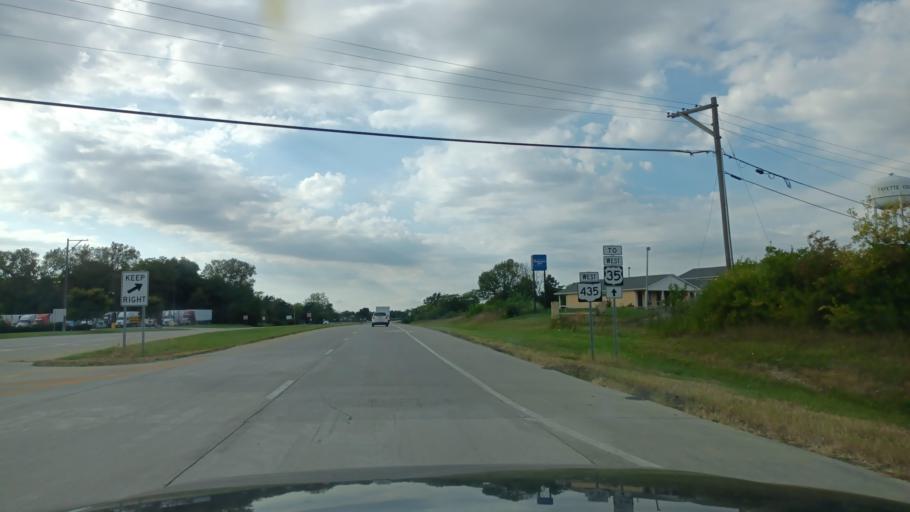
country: US
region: Ohio
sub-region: Fayette County
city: Jeffersonville
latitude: 39.6214
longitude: -83.6115
